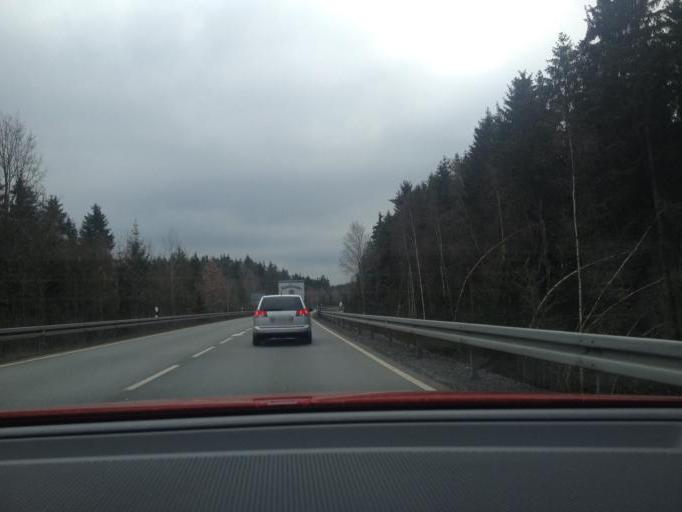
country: DE
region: Bavaria
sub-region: Upper Franconia
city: Rehau
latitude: 50.2695
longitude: 12.0178
